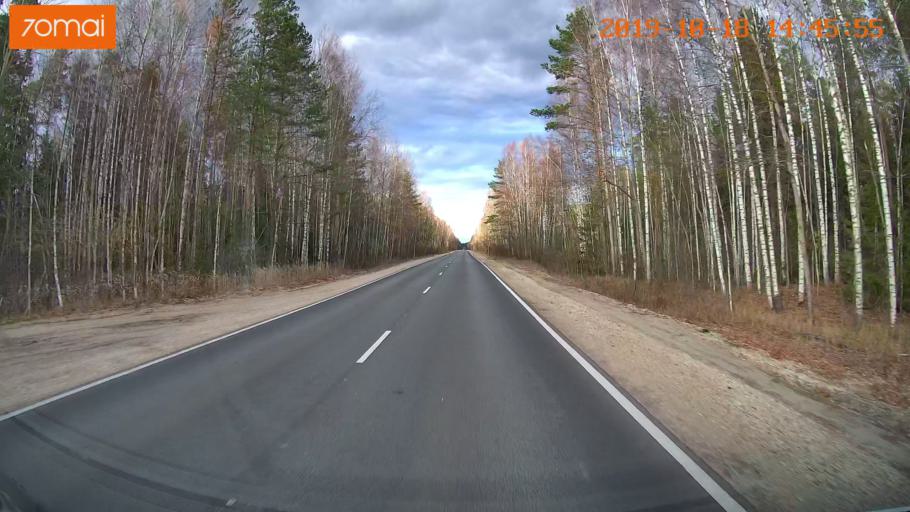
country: RU
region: Vladimir
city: Velikodvorskiy
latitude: 55.3628
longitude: 40.6799
